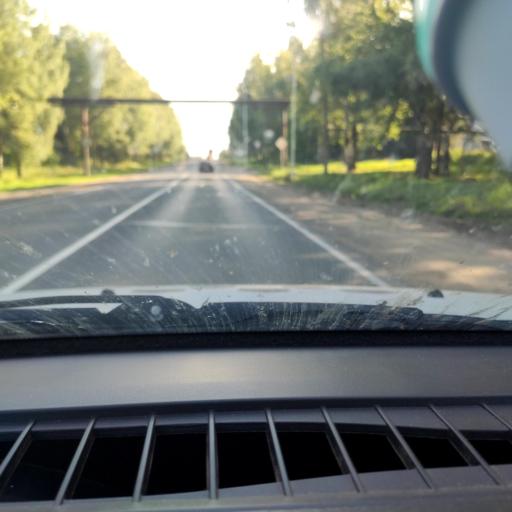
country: RU
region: Kirov
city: Vakhrushi
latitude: 58.6887
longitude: 50.0402
